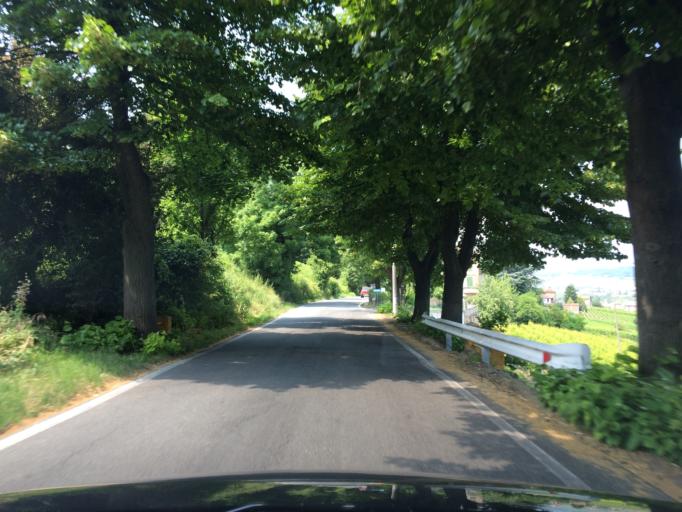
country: IT
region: Piedmont
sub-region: Provincia di Asti
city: Calosso
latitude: 44.7397
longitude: 8.2294
